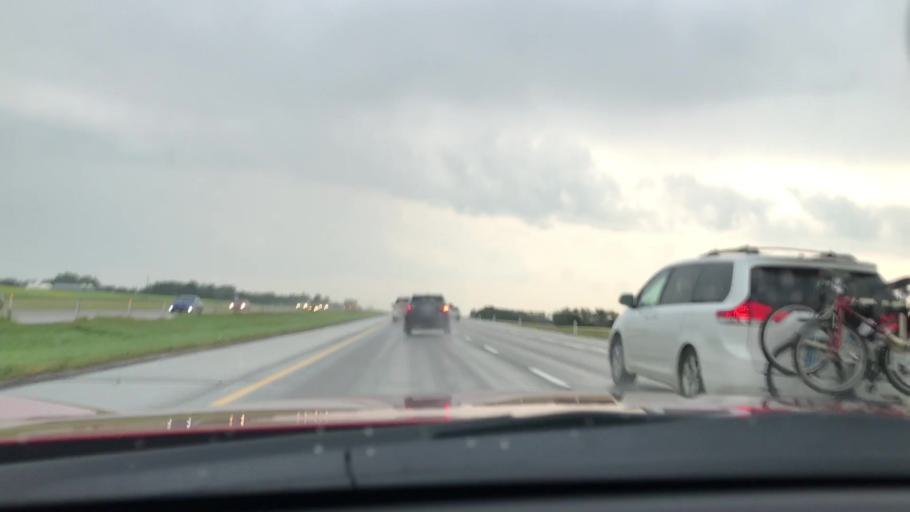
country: CA
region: Alberta
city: Penhold
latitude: 52.1578
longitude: -113.8140
